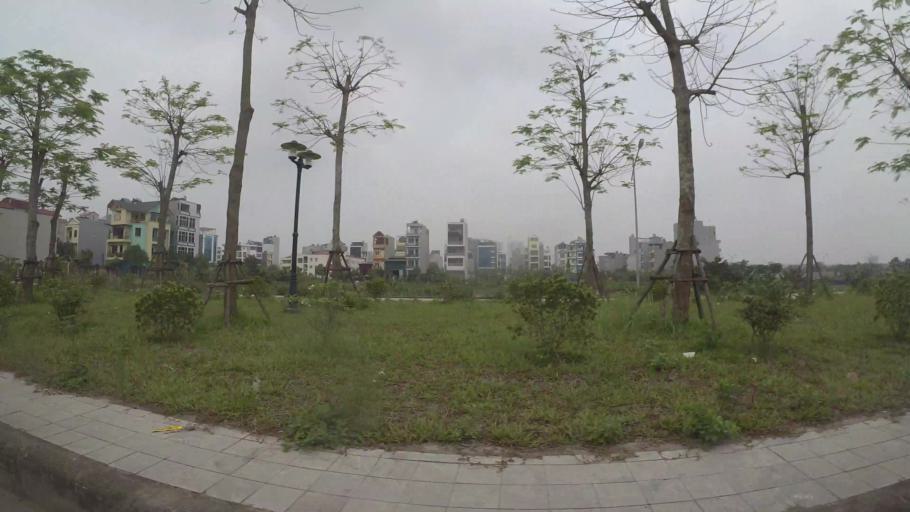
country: VN
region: Ha Noi
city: Ha Dong
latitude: 20.9738
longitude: 105.7505
